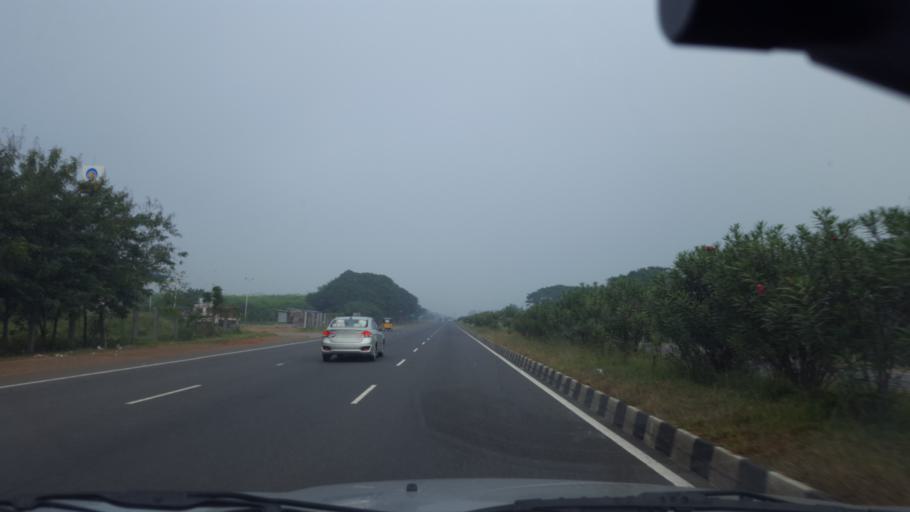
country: IN
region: Andhra Pradesh
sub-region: Prakasam
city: Ongole
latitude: 15.5912
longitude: 80.0351
